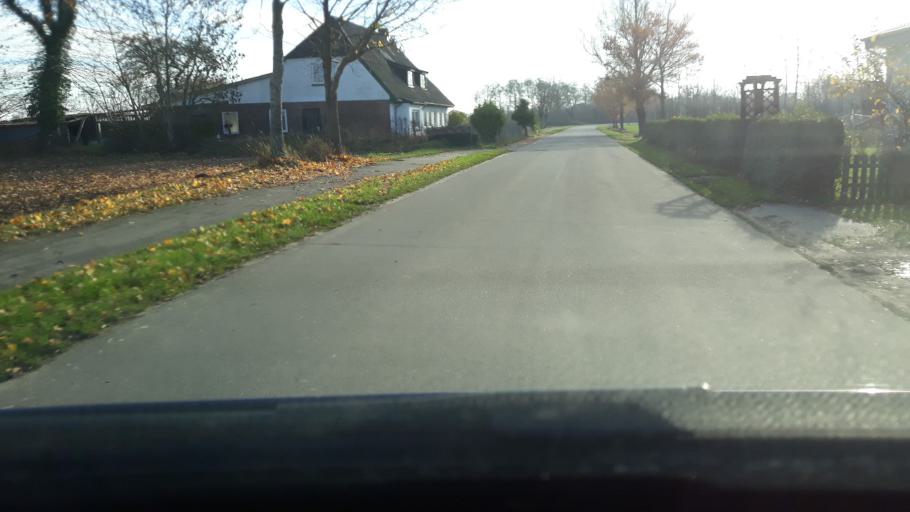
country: DE
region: Schleswig-Holstein
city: Brodersby
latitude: 54.6569
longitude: 10.0097
